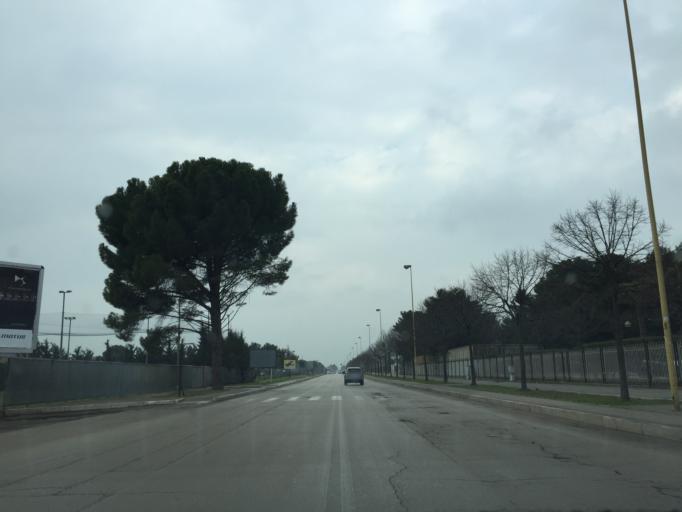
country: IT
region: Apulia
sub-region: Provincia di Foggia
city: Foggia
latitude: 41.4546
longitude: 15.5251
